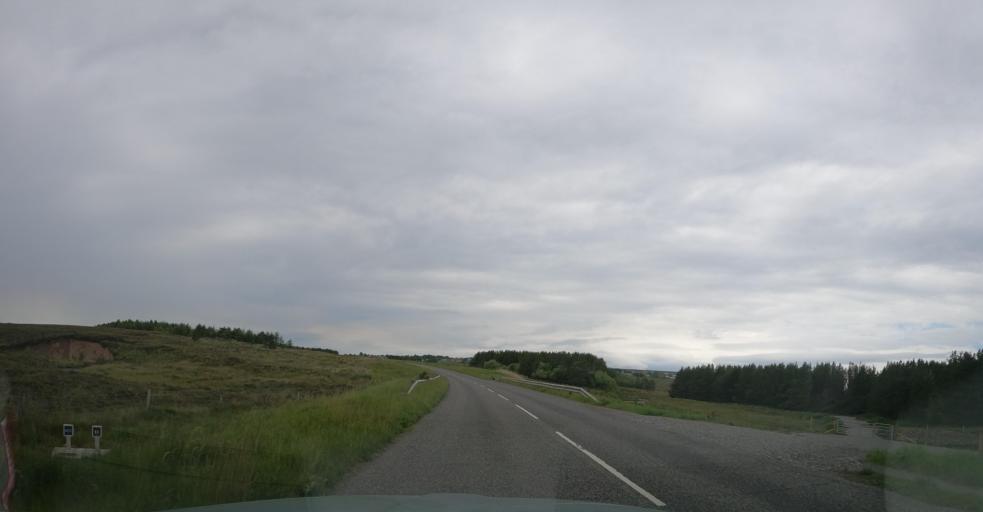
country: GB
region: Scotland
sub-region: Eilean Siar
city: Isle of Lewis
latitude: 58.2436
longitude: -6.3690
